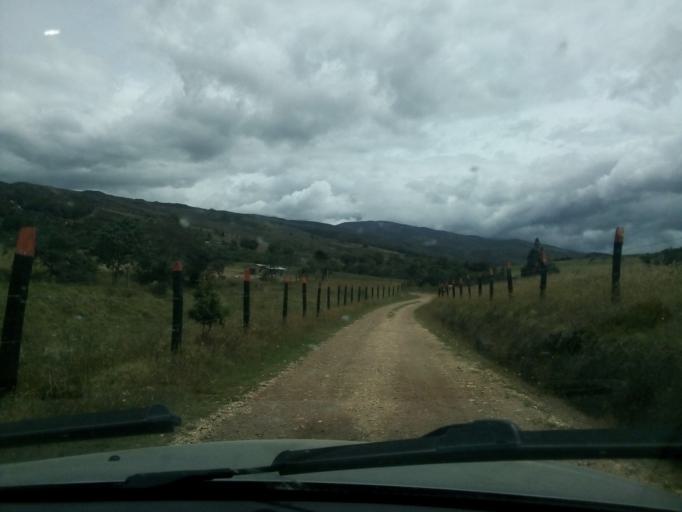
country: CO
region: Boyaca
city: Toca
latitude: 5.6144
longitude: -73.1150
